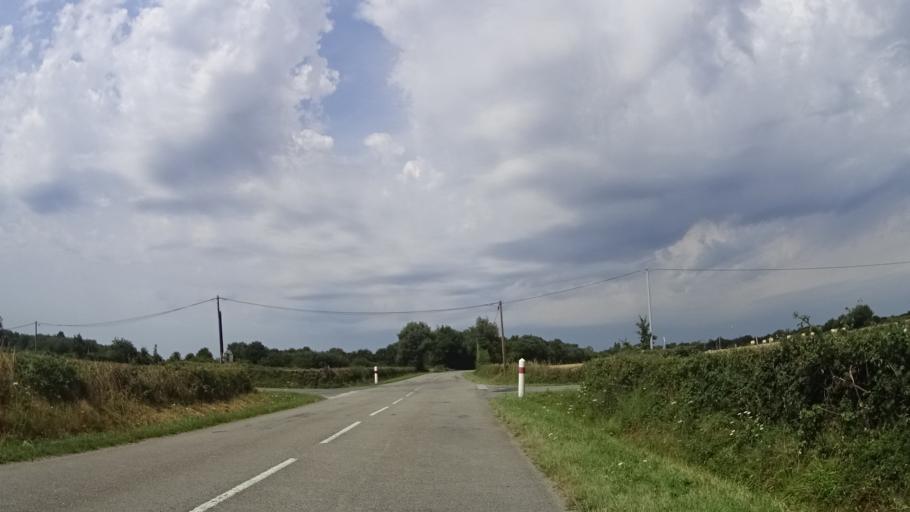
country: FR
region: Pays de la Loire
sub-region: Departement de la Loire-Atlantique
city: Heric
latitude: 47.4665
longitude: -1.6565
